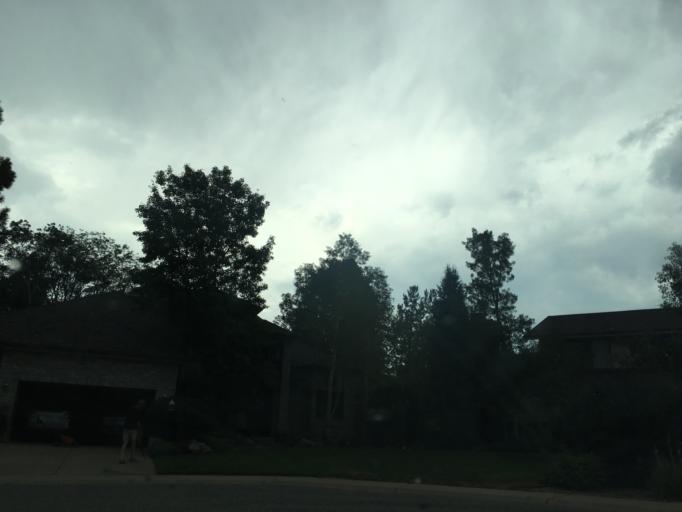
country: US
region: Colorado
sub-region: Arapahoe County
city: Sheridan
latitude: 39.6625
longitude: -105.0340
